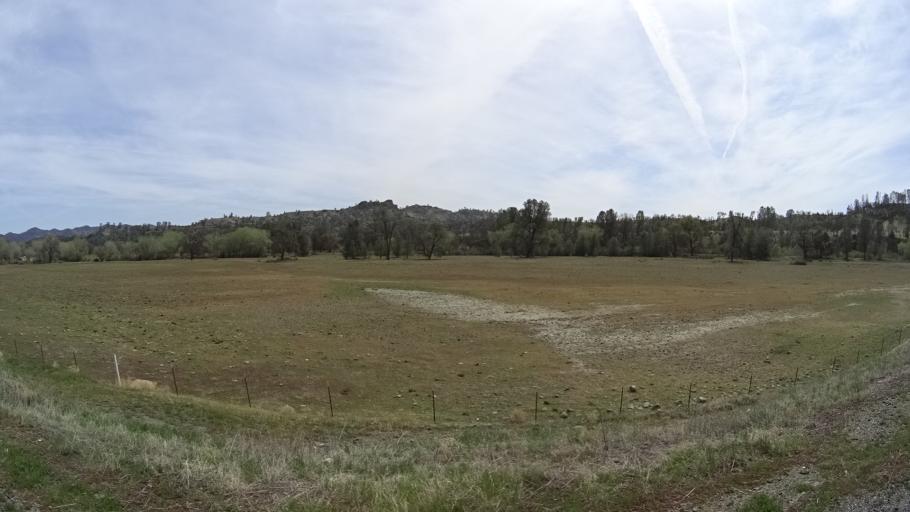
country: US
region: California
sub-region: Glenn County
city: Willows
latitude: 39.4236
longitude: -122.5322
